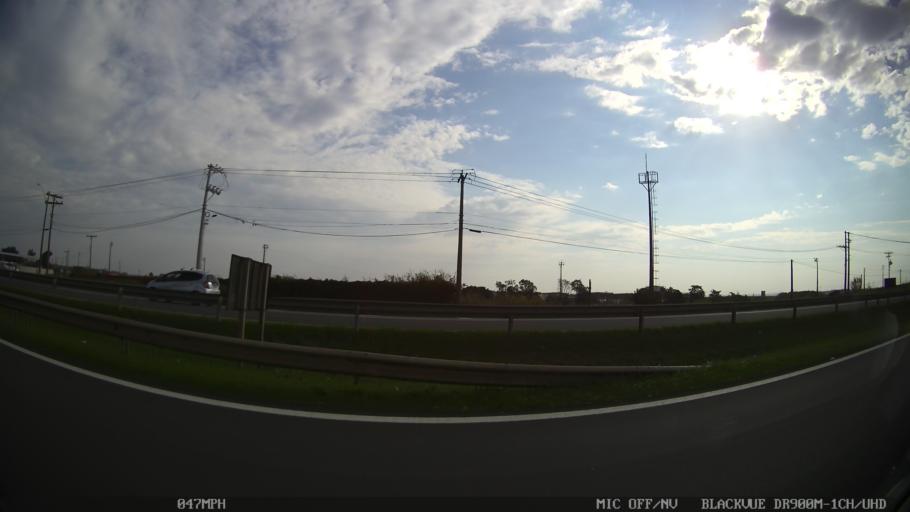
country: BR
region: Sao Paulo
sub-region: Paulinia
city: Paulinia
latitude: -22.7149
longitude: -47.1428
